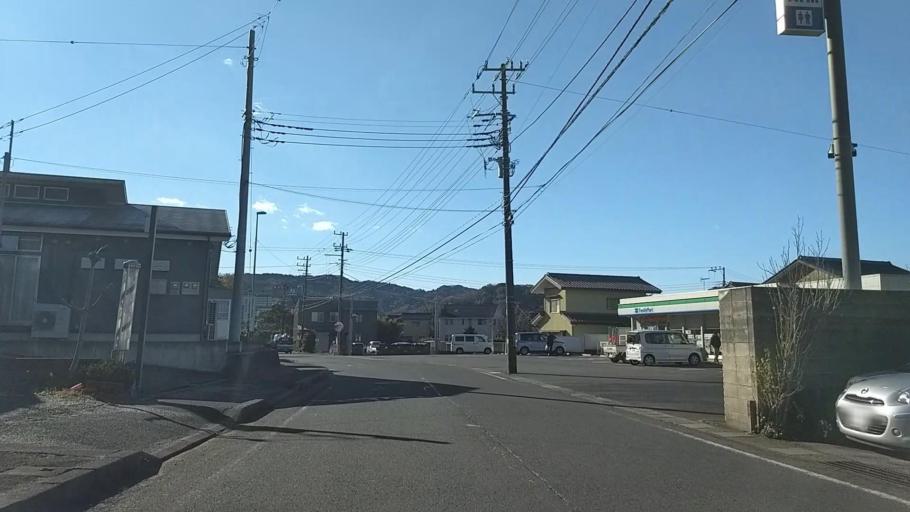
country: JP
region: Chiba
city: Futtsu
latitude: 35.2201
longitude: 139.8726
